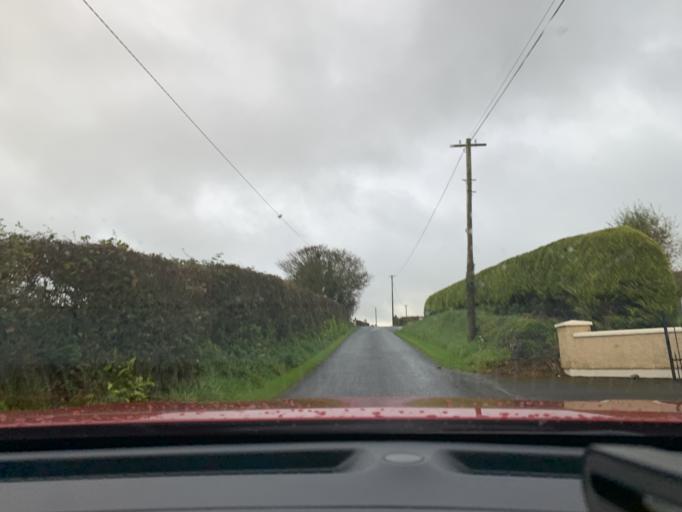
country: IE
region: Connaught
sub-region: Sligo
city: Ballymote
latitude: 54.1298
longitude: -8.5239
